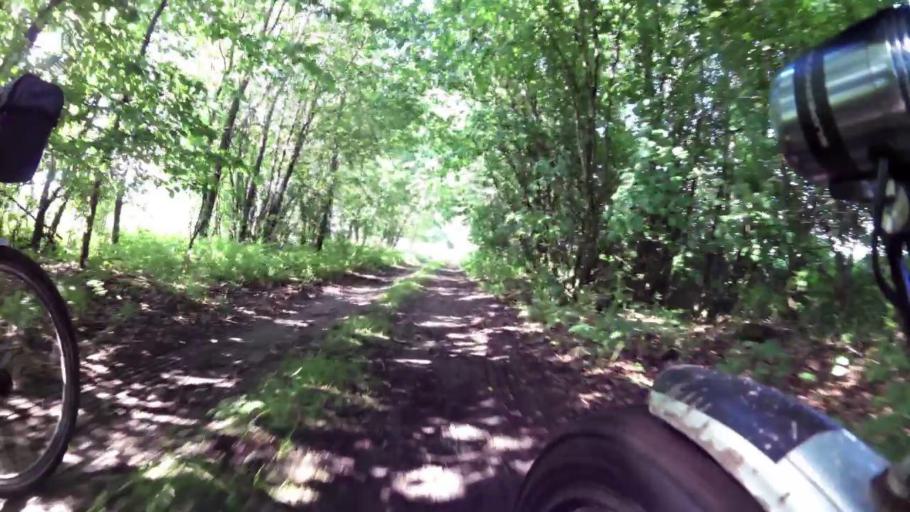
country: PL
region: West Pomeranian Voivodeship
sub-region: Powiat swidwinski
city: Swidwin
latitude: 53.7422
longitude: 15.7566
